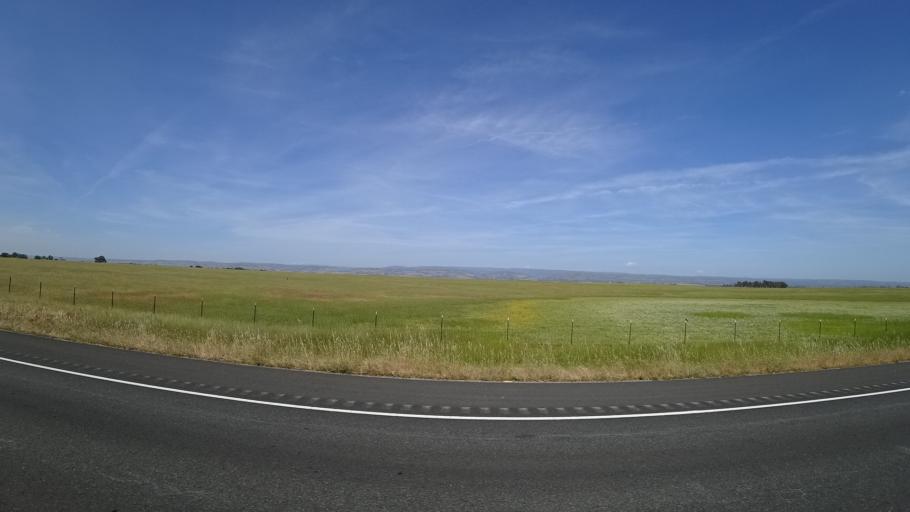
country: US
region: California
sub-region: Glenn County
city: Hamilton City
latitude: 39.8665
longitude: -121.9631
